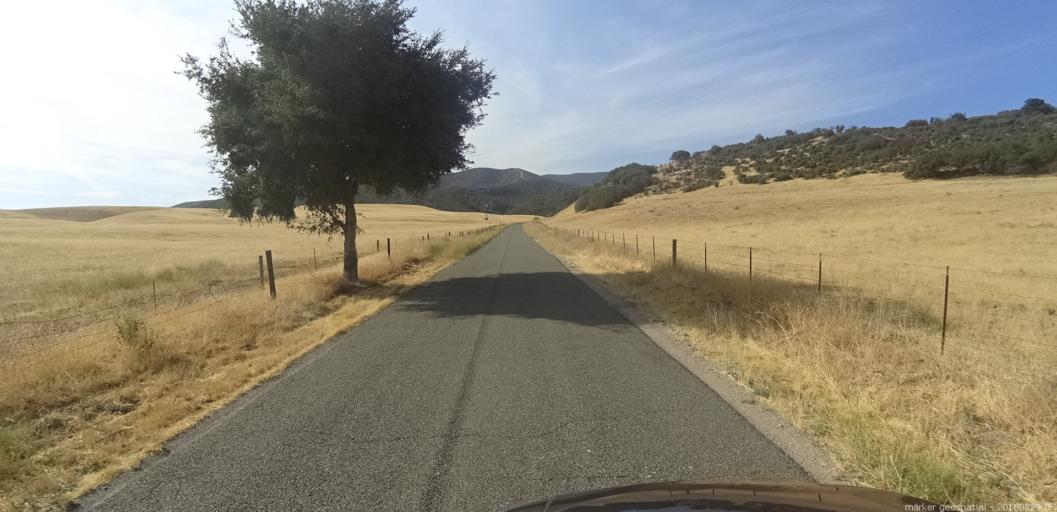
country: US
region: California
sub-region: Monterey County
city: King City
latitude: 36.0539
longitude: -121.0527
